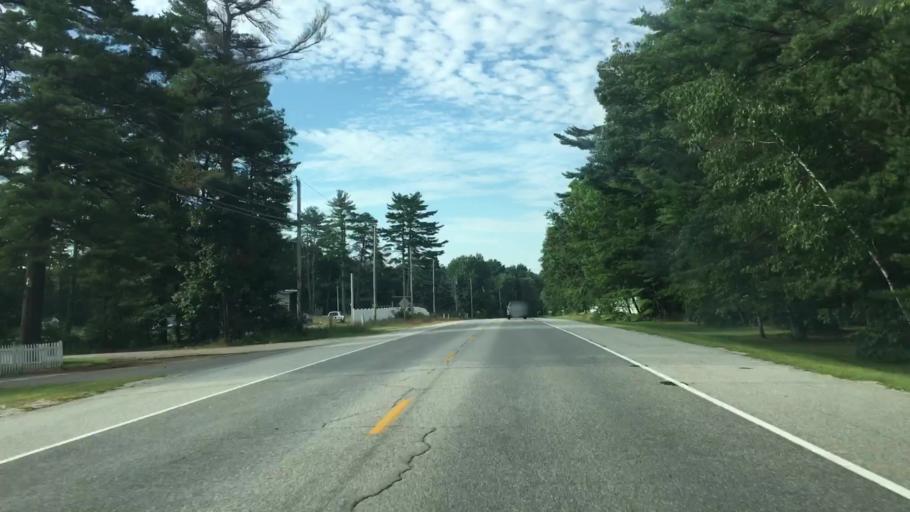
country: US
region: Maine
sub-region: Cumberland County
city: Raymond
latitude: 43.8713
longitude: -70.4649
